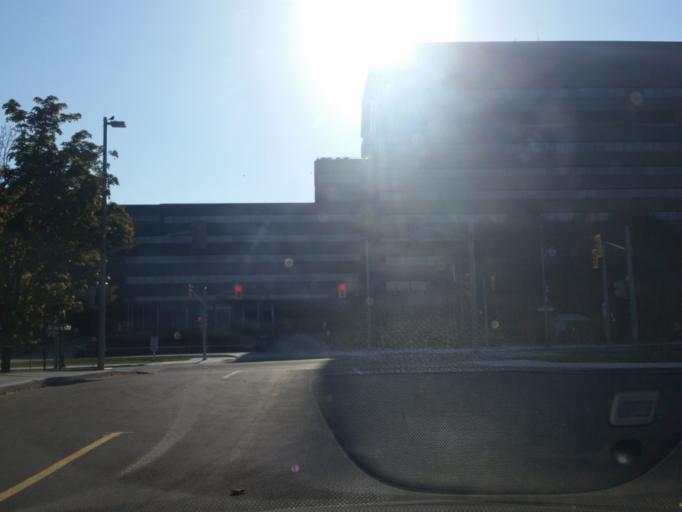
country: CA
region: Ontario
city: Ottawa
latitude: 45.4373
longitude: -75.6981
